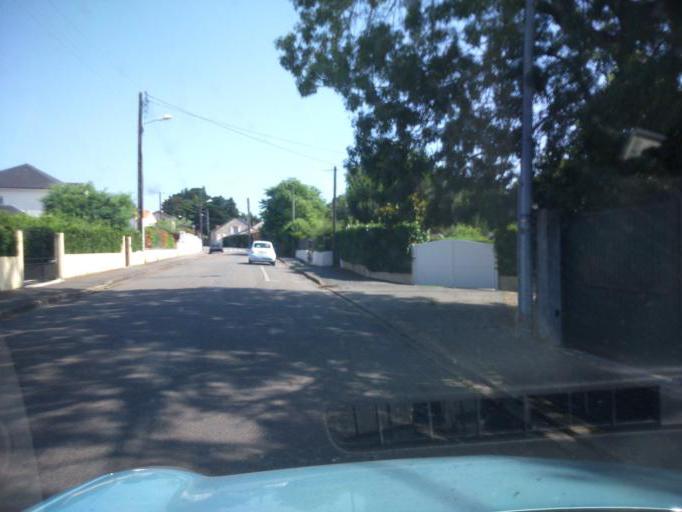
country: FR
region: Pays de la Loire
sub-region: Departement de la Loire-Atlantique
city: Saint-Sebastien-sur-Loire
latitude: 47.2028
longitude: -1.5197
